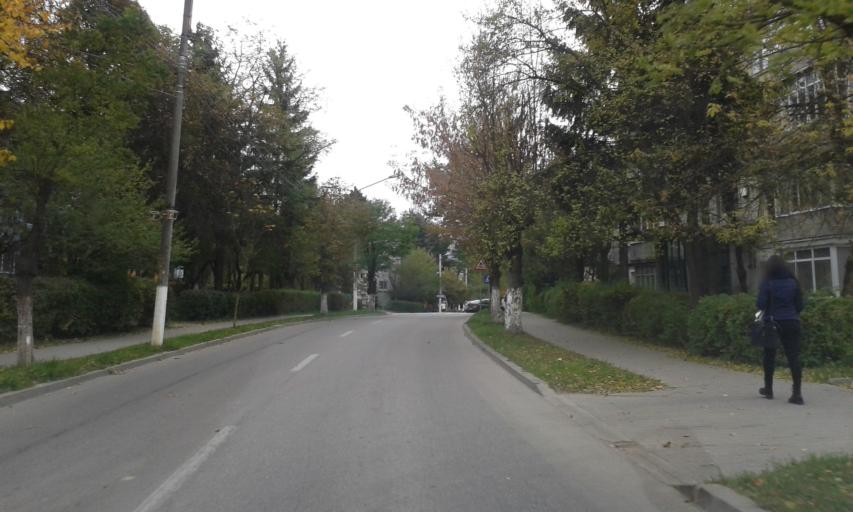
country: RO
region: Hunedoara
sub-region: Municipiul Petrosani
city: Petrosani
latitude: 45.4059
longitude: 23.3747
